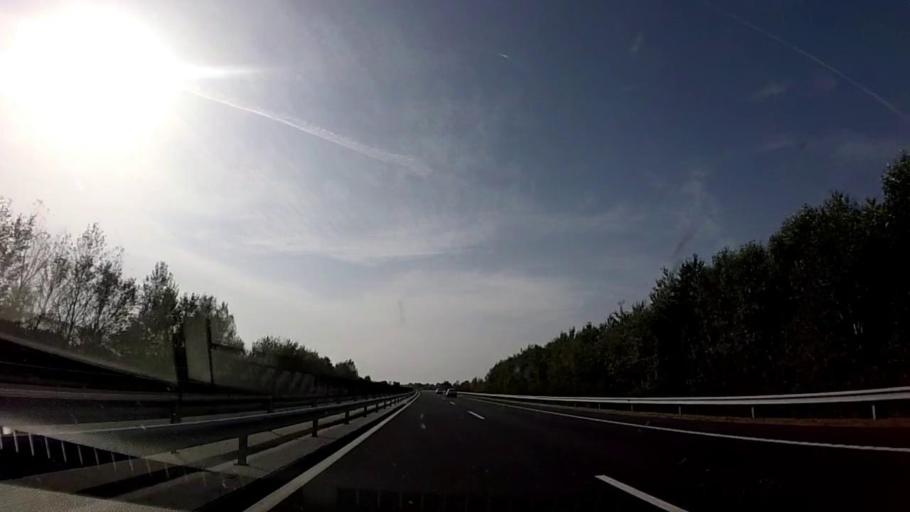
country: HU
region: Zala
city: Zalakomar
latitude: 46.5481
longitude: 17.2142
